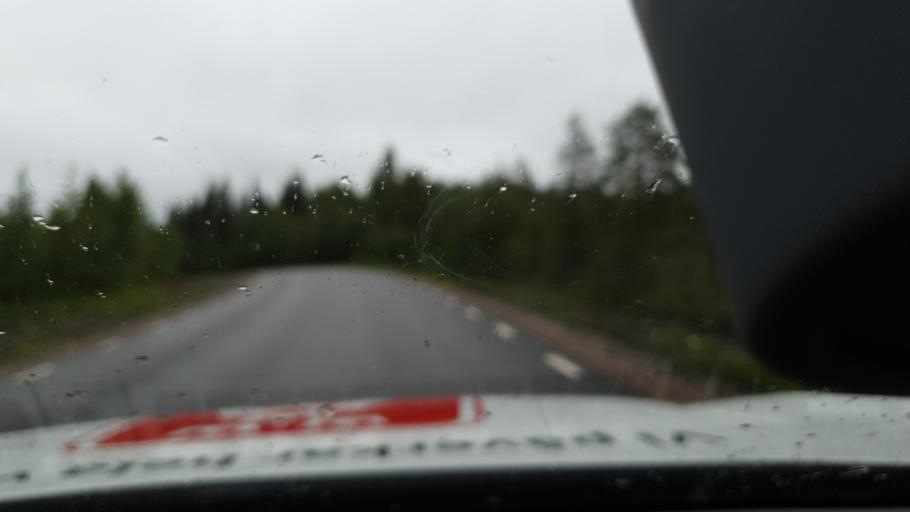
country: SE
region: Norrbotten
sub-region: Overtornea Kommun
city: OEvertornea
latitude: 66.5433
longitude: 23.3564
